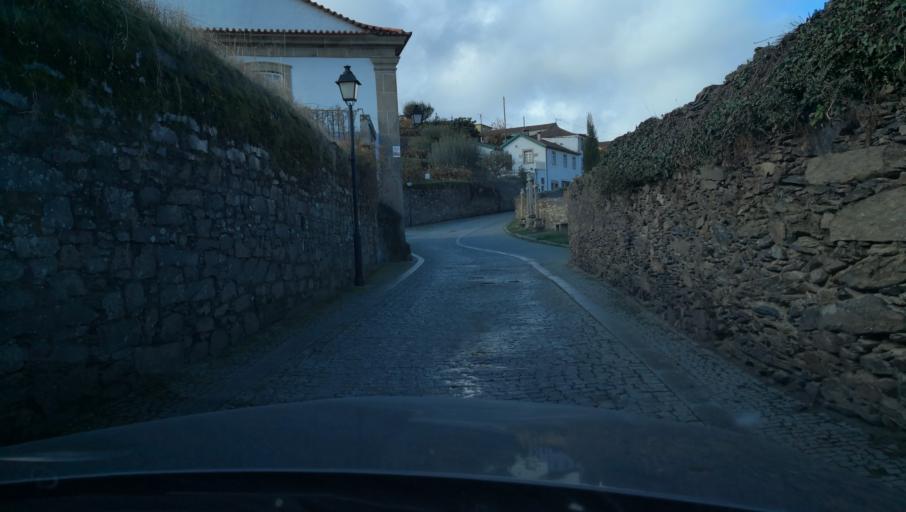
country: PT
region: Vila Real
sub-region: Sabrosa
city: Vilela
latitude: 41.2182
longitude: -7.5690
